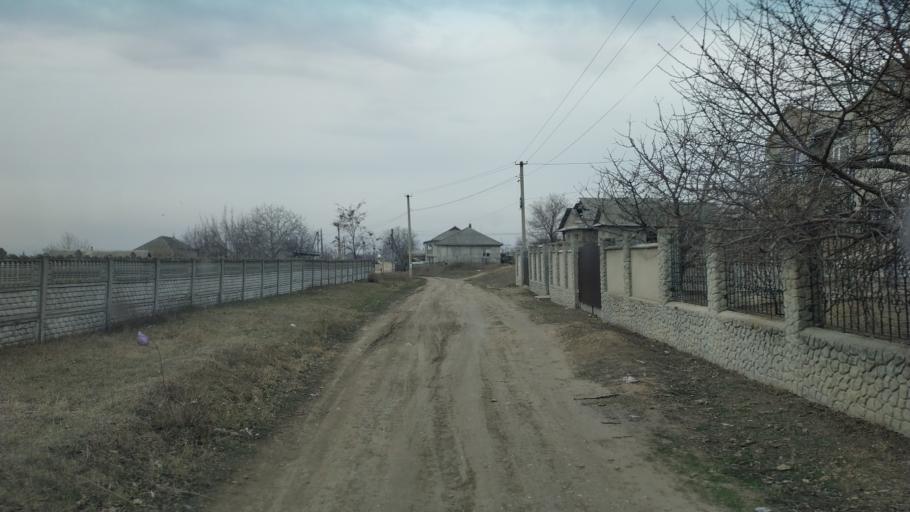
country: MD
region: Chisinau
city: Singera
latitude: 46.9375
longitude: 28.9895
